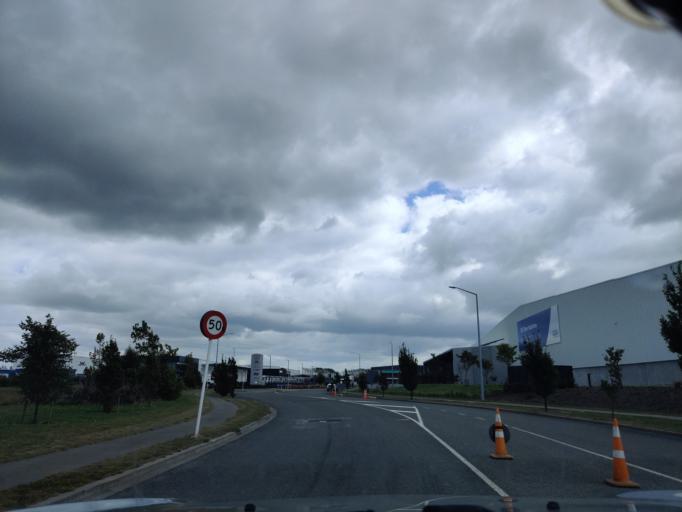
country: NZ
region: Canterbury
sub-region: Selwyn District
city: Prebbleton
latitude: -43.5554
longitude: 172.5118
